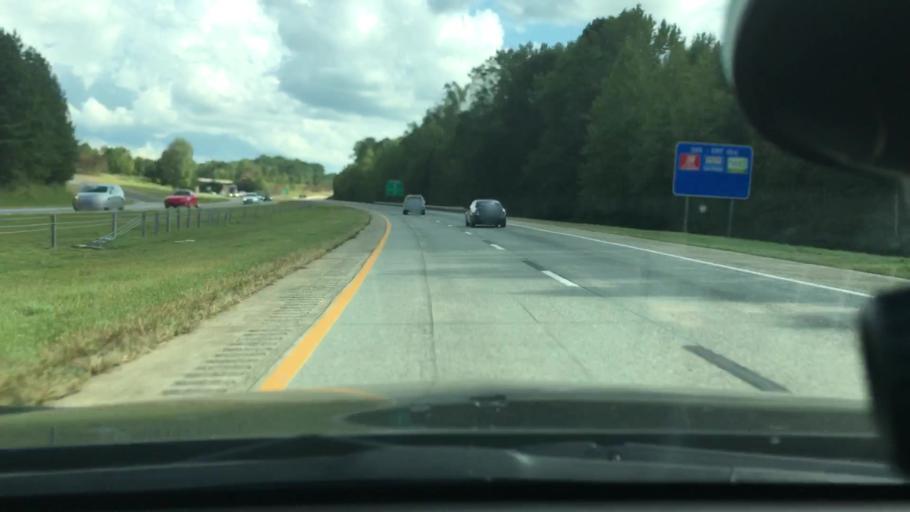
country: US
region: North Carolina
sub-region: Orange County
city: Chapel Hill
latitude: 35.9743
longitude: -79.0679
